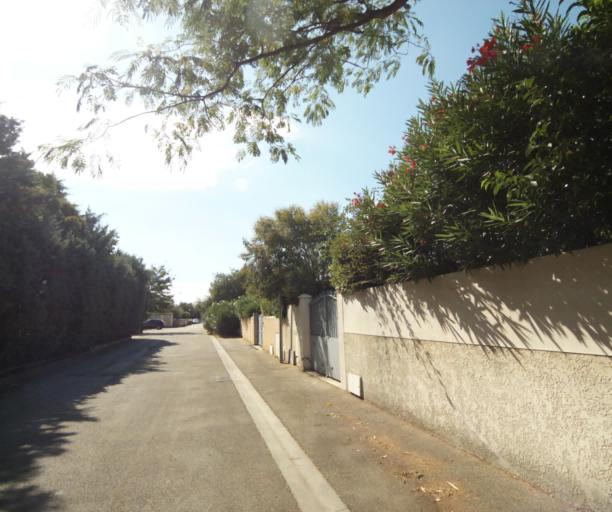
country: FR
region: Languedoc-Roussillon
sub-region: Departement du Gard
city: Bouillargues
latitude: 43.7965
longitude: 4.4372
